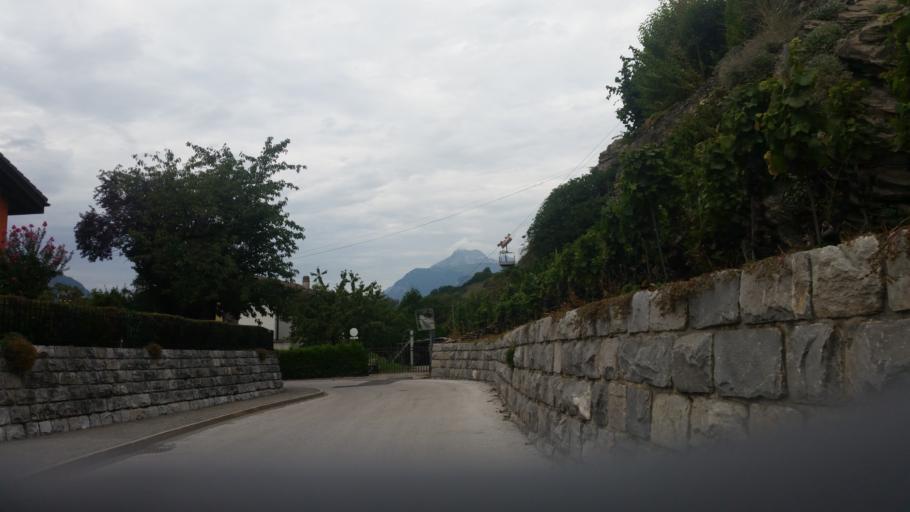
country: CH
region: Valais
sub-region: Conthey District
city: Conthey
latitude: 46.2230
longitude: 7.3254
